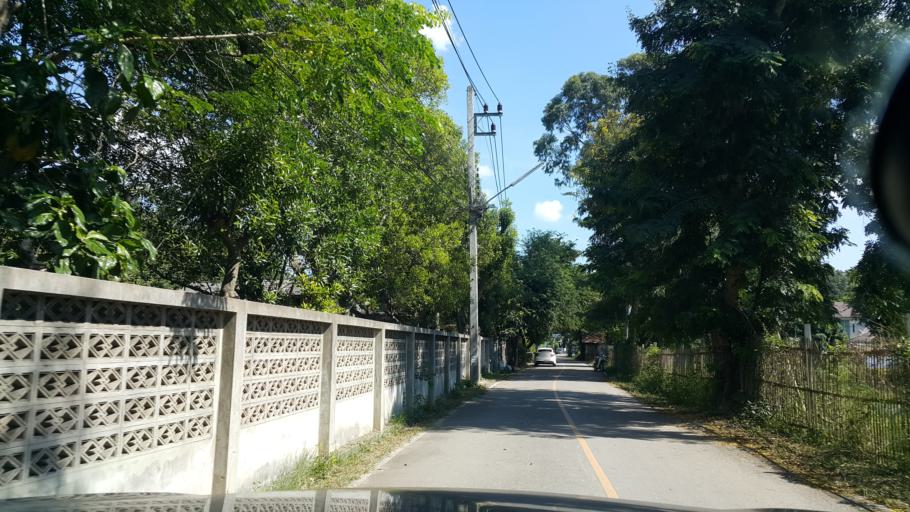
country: TH
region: Chiang Mai
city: Chiang Mai
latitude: 18.7410
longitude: 98.9722
